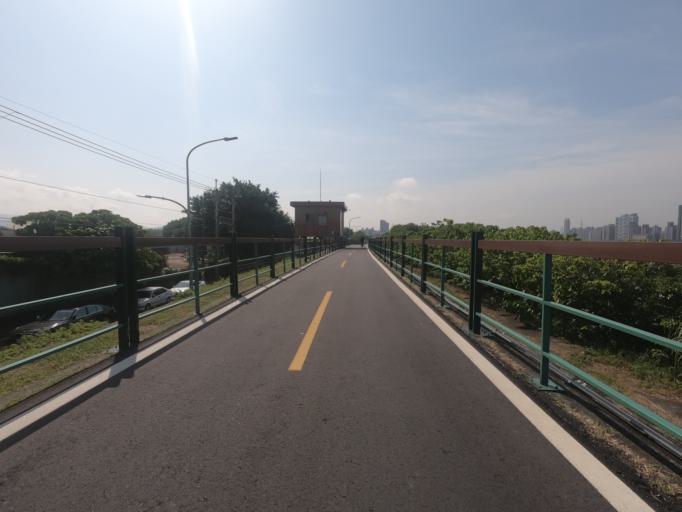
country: TW
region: Taipei
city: Taipei
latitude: 25.0988
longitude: 121.4907
